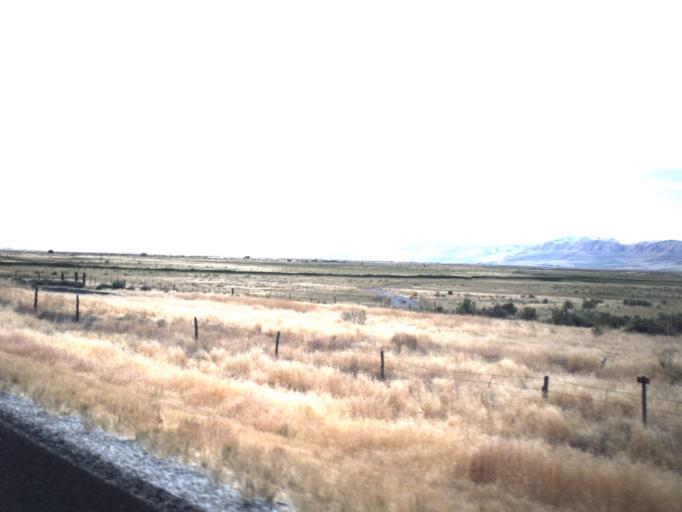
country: US
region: Utah
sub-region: Box Elder County
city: Tremonton
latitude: 41.6318
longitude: -112.4194
